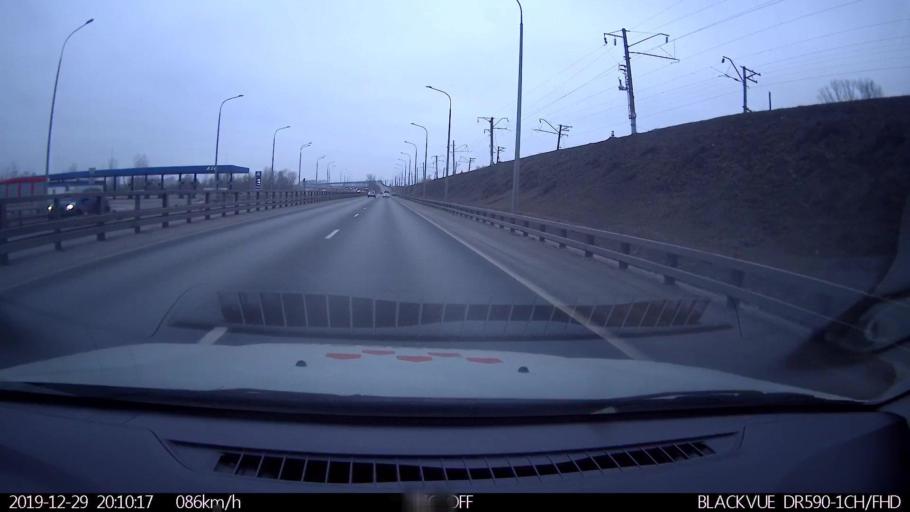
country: RU
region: Nizjnij Novgorod
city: Neklyudovo
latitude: 56.3659
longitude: 43.9371
